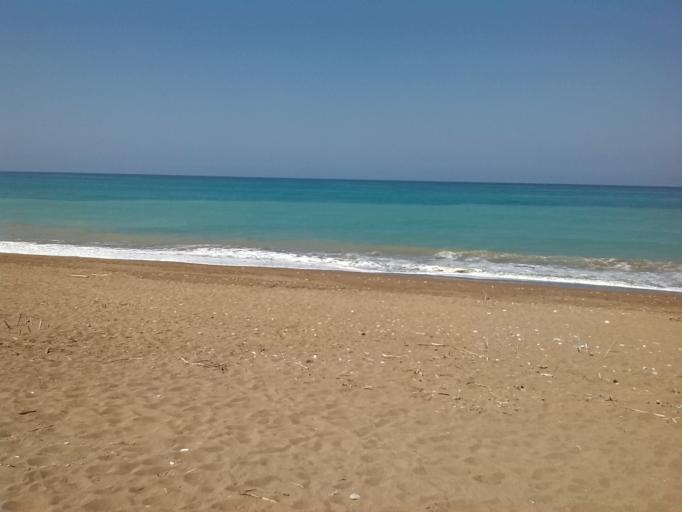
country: GR
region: Peloponnese
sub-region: Nomos Messinias
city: Kyparissia
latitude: 37.3695
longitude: 21.6853
